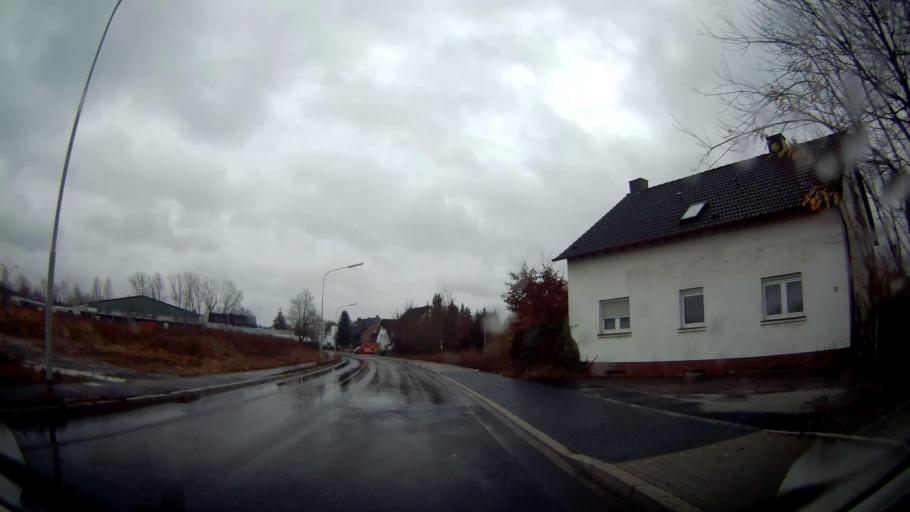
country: DE
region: North Rhine-Westphalia
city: Bochum-Hordel
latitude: 51.5214
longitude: 7.1978
